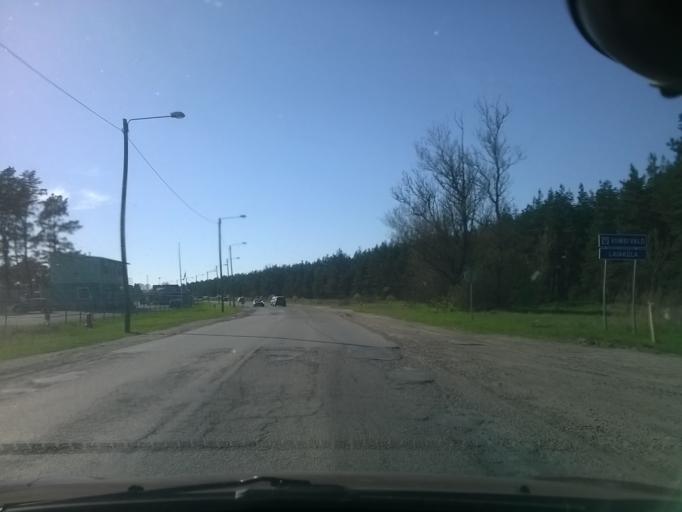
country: EE
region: Harju
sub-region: Joelaehtme vald
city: Loo
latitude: 59.4610
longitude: 24.9232
